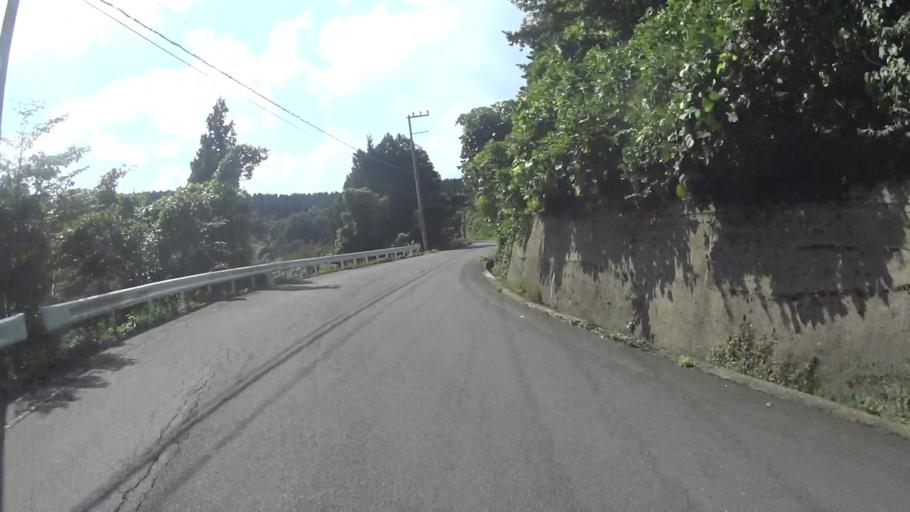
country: JP
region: Kyoto
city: Miyazu
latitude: 35.7097
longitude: 135.1933
